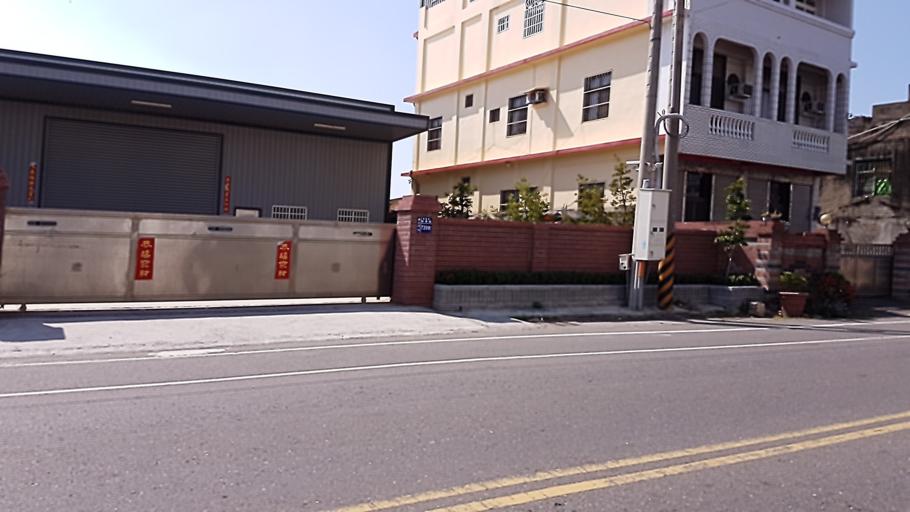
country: TW
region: Taiwan
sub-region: Changhua
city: Chang-hua
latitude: 24.0808
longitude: 120.5151
